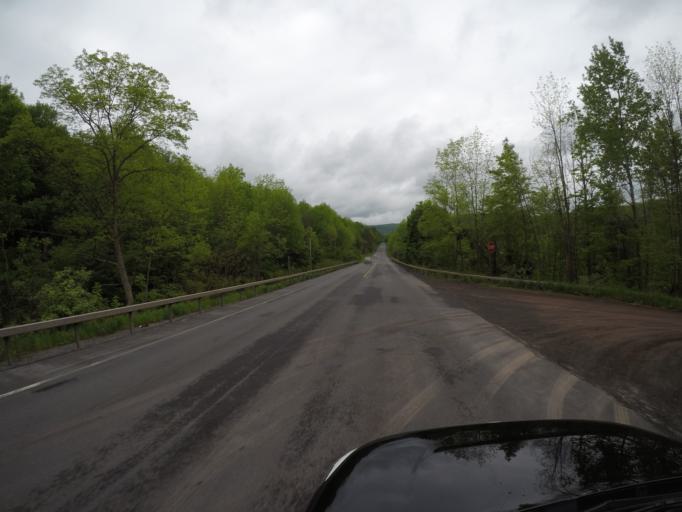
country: US
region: New York
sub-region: Delaware County
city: Delhi
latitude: 42.2407
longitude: -74.7972
